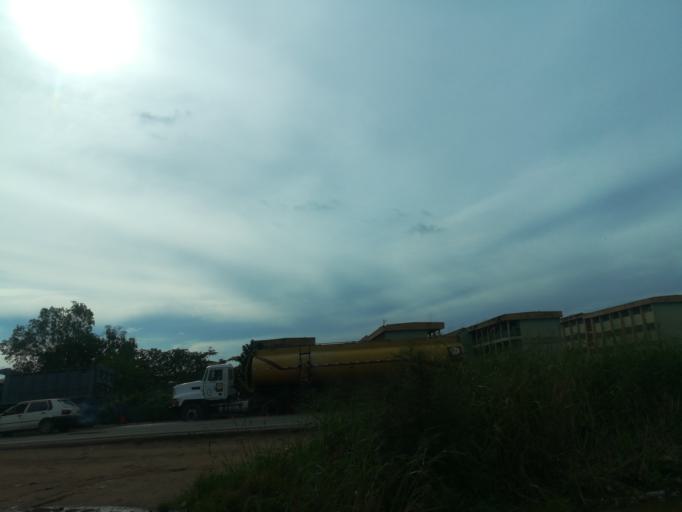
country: NG
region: Oyo
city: Ibadan
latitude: 7.3874
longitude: 3.9352
